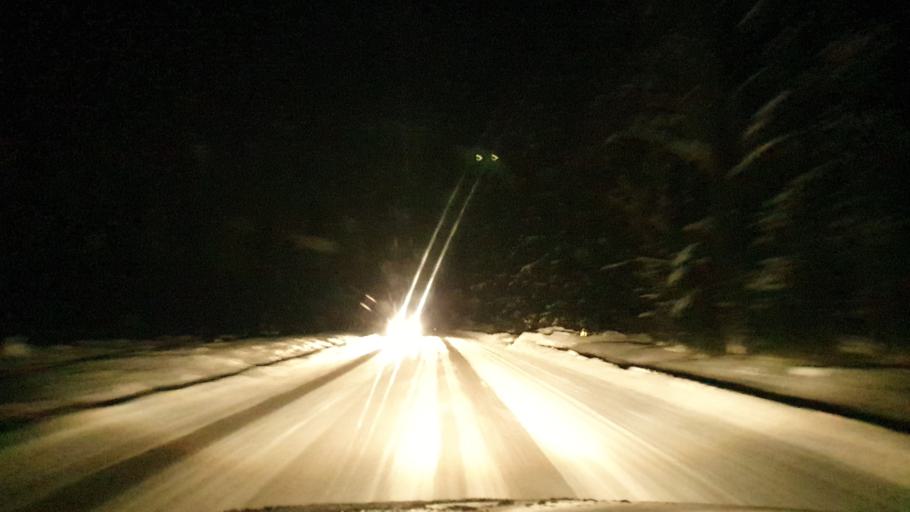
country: EE
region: Vorumaa
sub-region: Antsla vald
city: Vana-Antsla
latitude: 57.9709
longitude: 26.7589
